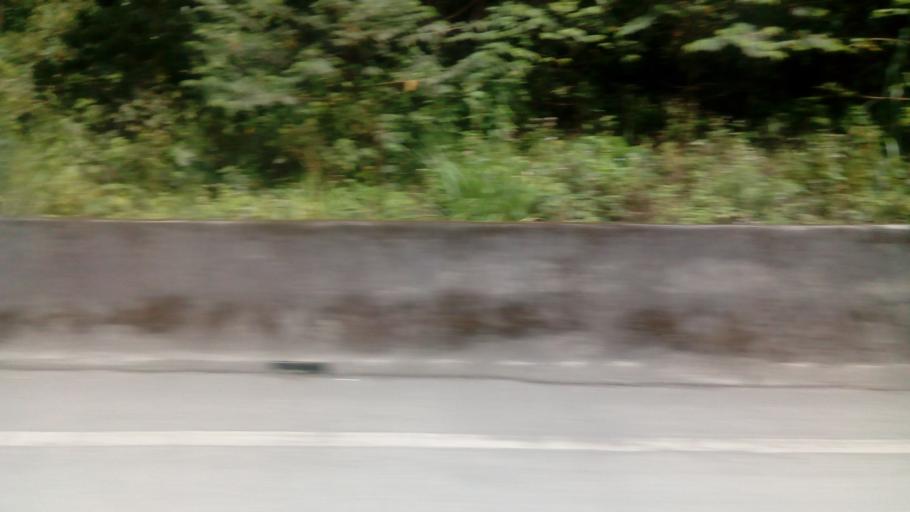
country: TW
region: Taiwan
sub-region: Yilan
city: Yilan
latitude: 24.5595
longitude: 121.4772
